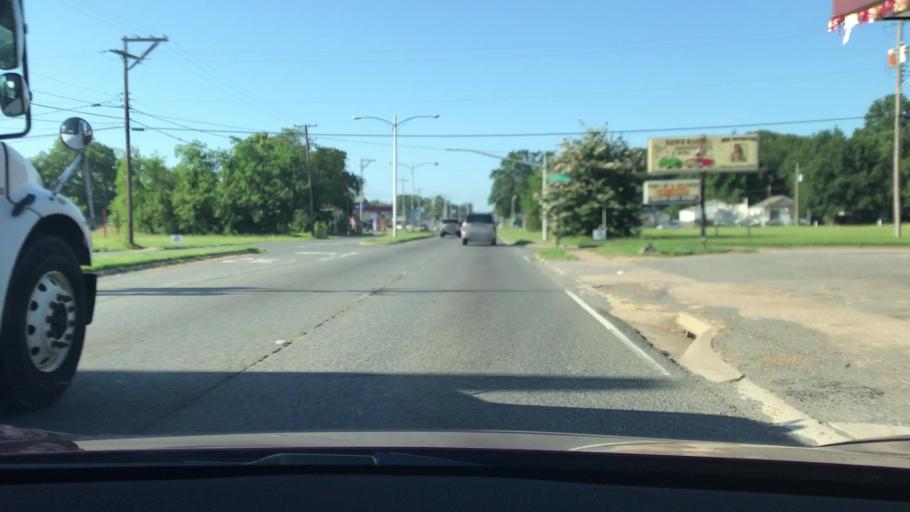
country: US
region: Louisiana
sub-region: Caddo Parish
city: Shreveport
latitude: 32.4749
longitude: -93.7801
